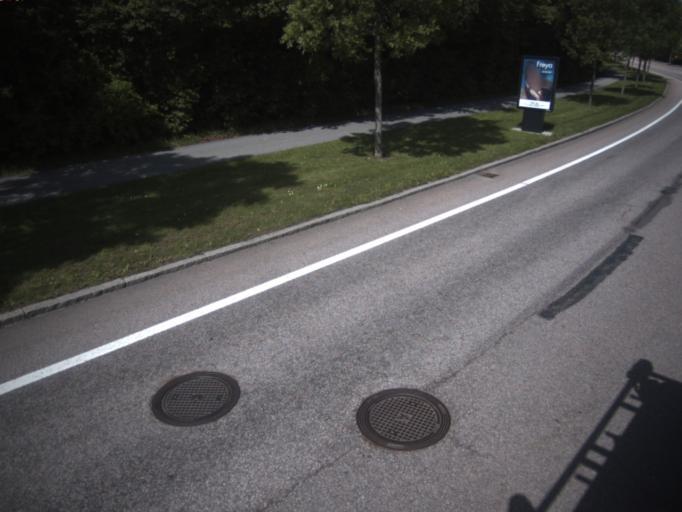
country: SE
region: Skane
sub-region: Helsingborg
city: Helsingborg
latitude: 56.0583
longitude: 12.7178
